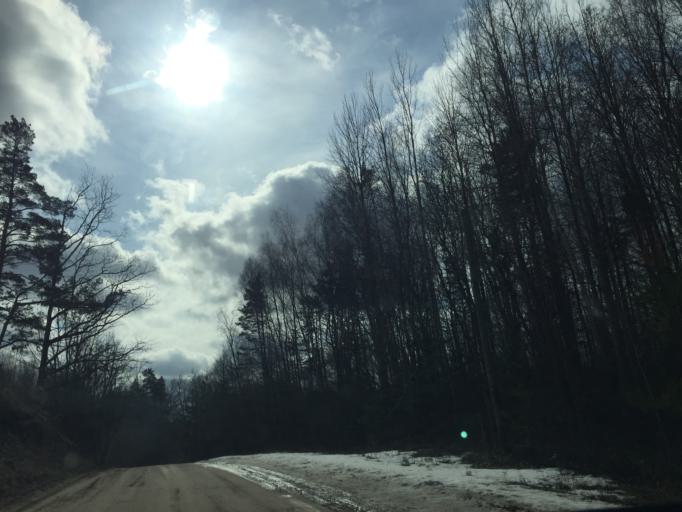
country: LV
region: Vecumnieki
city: Vecumnieki
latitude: 56.5867
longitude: 24.5616
